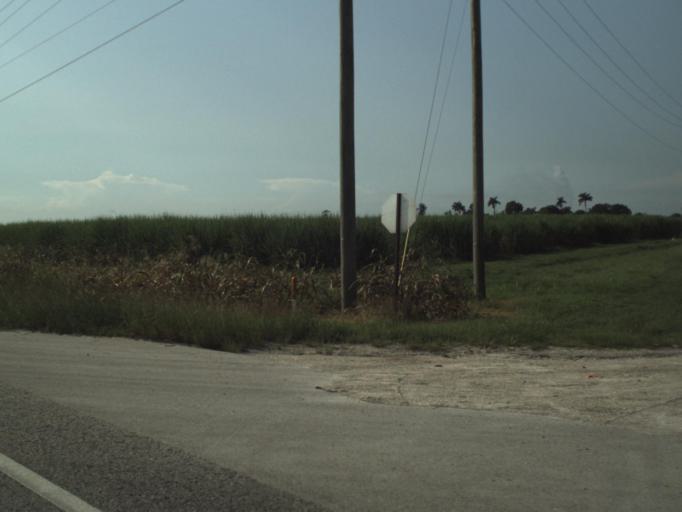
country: US
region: Florida
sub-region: Palm Beach County
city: South Bay
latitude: 26.6938
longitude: -80.7729
